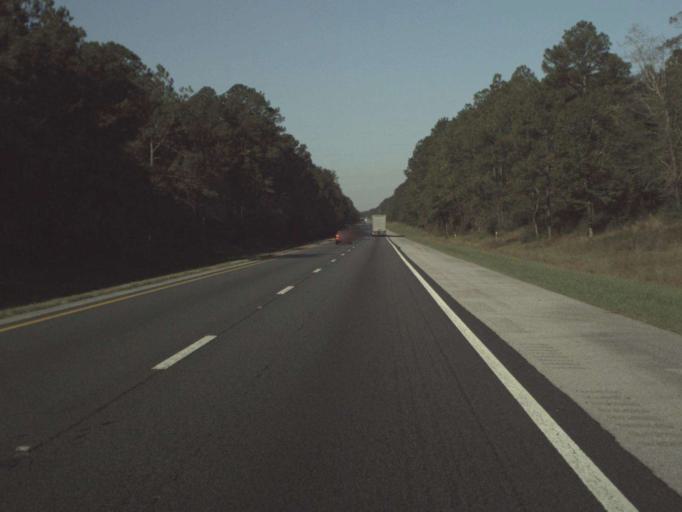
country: US
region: Florida
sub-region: Holmes County
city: Bonifay
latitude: 30.7612
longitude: -85.7632
